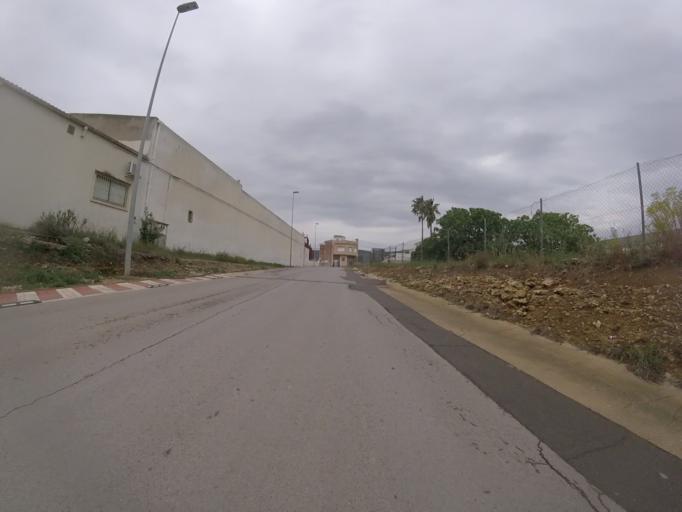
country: ES
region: Valencia
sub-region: Provincia de Castello
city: Alcala de Xivert
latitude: 40.3082
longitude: 0.2294
